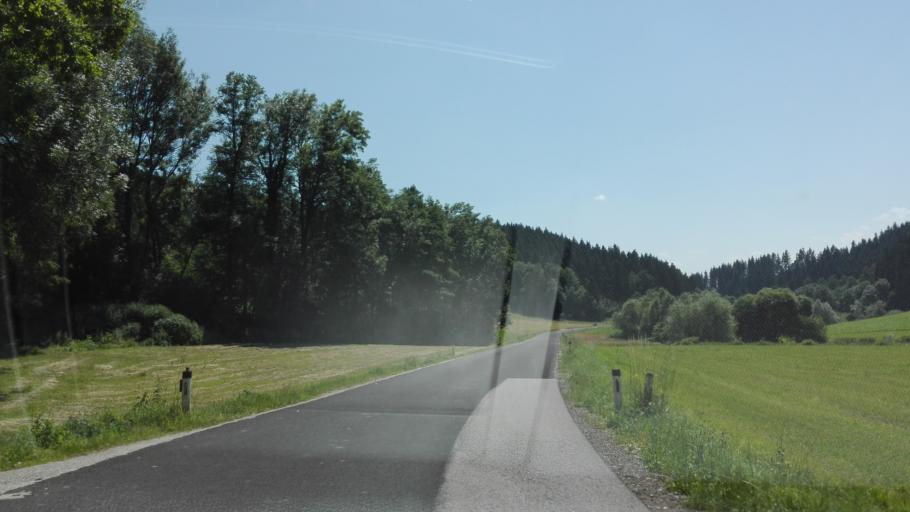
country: AT
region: Upper Austria
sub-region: Politischer Bezirk Grieskirchen
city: Bad Schallerbach
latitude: 48.3589
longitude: 13.8908
